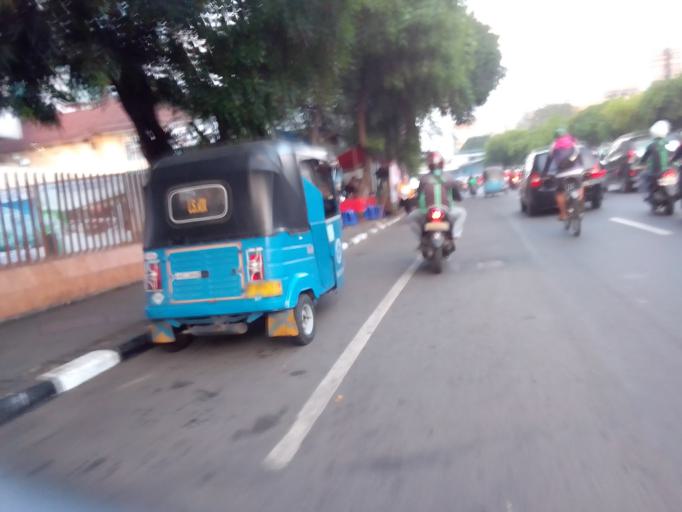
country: ID
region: Jakarta Raya
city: Jakarta
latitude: -6.1956
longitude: 106.8502
